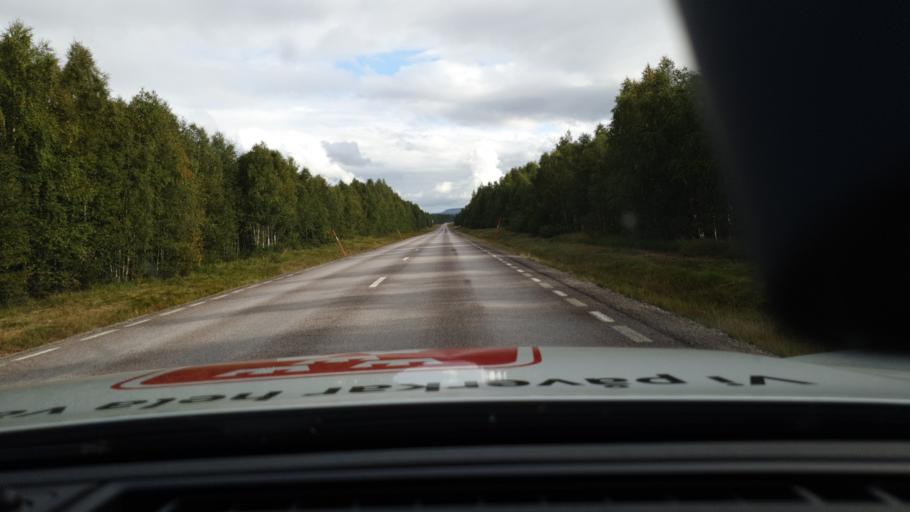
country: SE
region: Norrbotten
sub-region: Gallivare Kommun
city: Gaellivare
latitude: 66.9088
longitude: 21.5717
